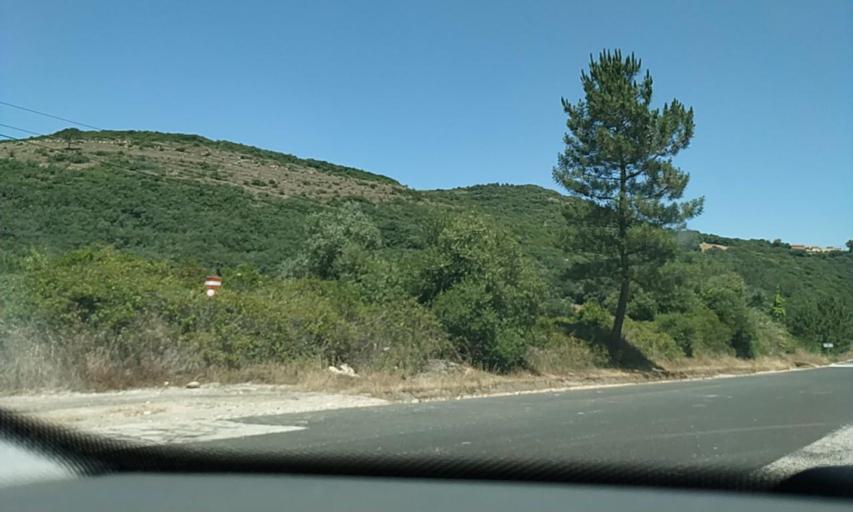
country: PT
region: Lisbon
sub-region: Sintra
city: Almargem
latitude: 38.8767
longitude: -9.2475
